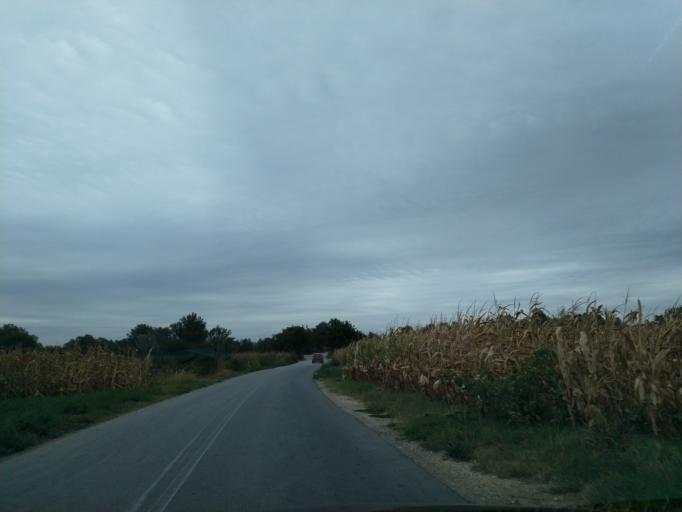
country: RS
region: Central Serbia
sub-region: Pomoravski Okrug
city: Paracin
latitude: 43.8297
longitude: 21.3389
